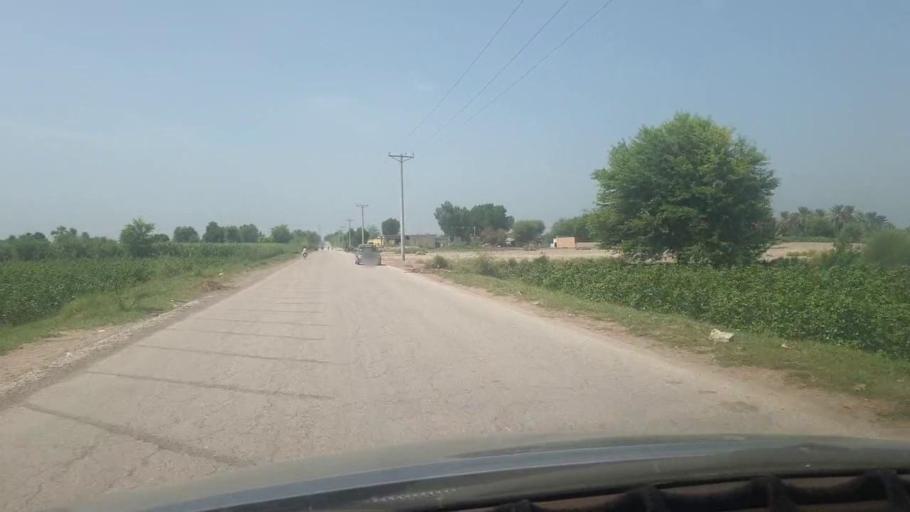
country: PK
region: Sindh
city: Ranipur
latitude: 27.2922
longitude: 68.6067
